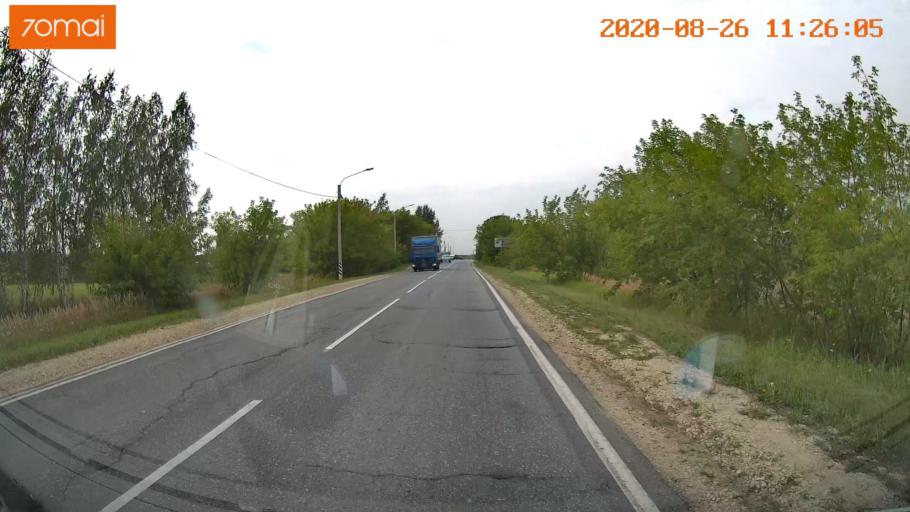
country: RU
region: Rjazan
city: Shilovo
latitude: 54.3365
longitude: 40.9541
